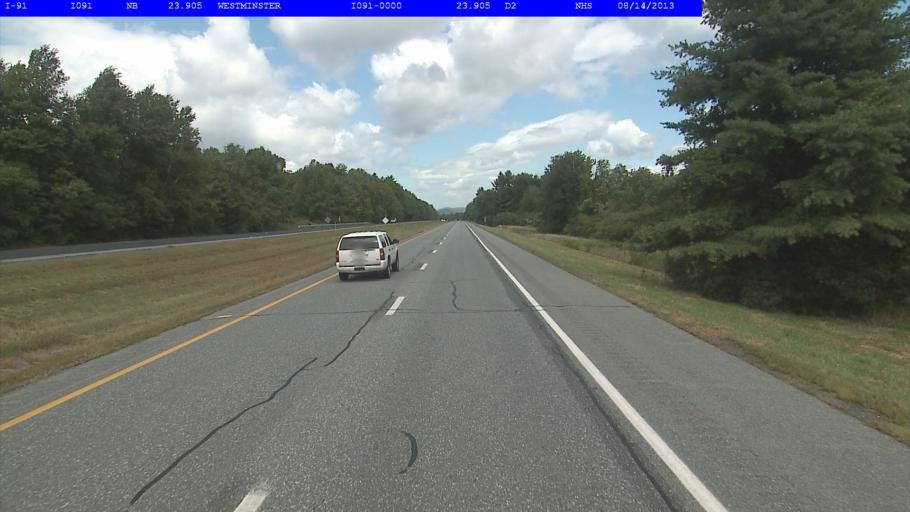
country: US
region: New Hampshire
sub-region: Cheshire County
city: Westmoreland
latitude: 43.0254
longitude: -72.4715
